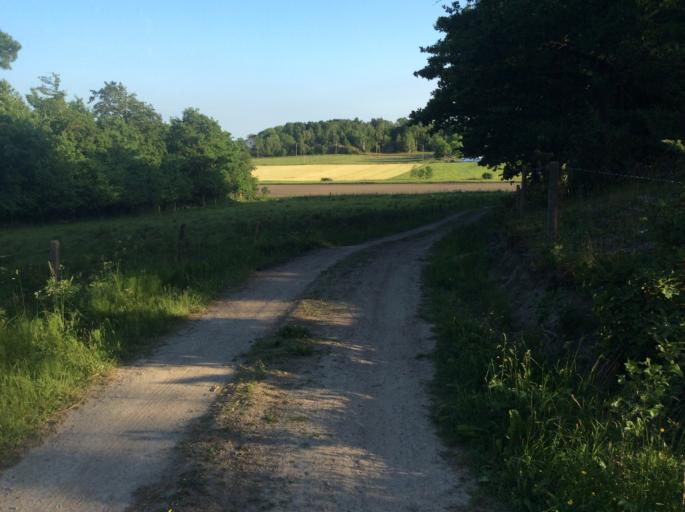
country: SE
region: Vaestra Goetaland
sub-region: Goteborg
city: Torslanda
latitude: 57.7943
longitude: 11.8577
